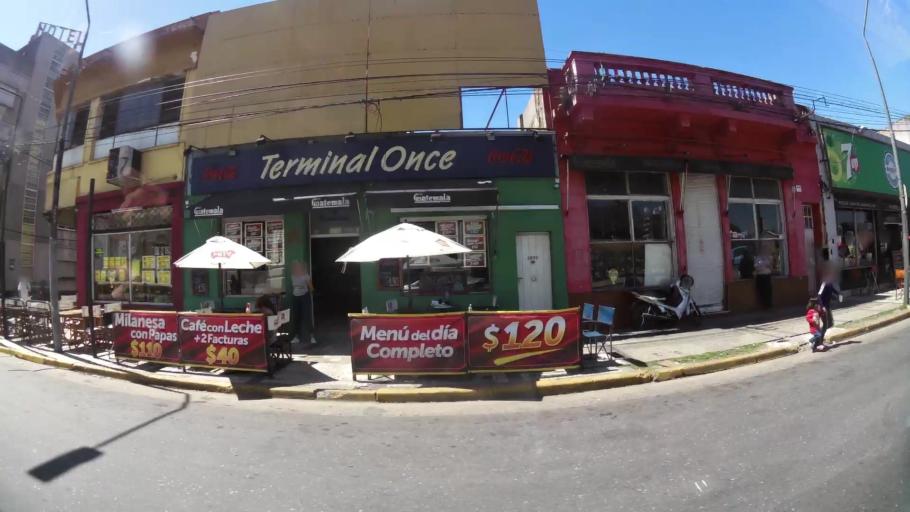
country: AR
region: Santa Fe
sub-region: Departamento de Rosario
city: Rosario
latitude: -32.9391
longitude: -60.6711
